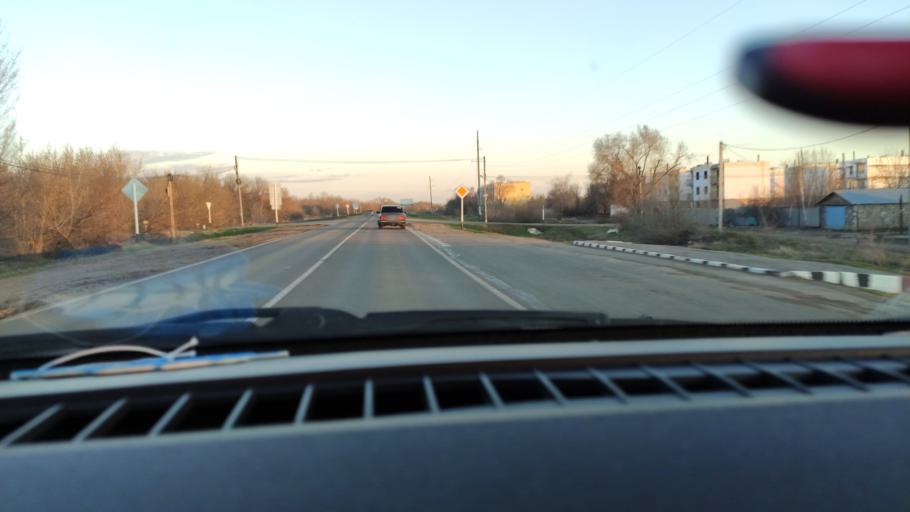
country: RU
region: Saratov
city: Privolzhskiy
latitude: 51.3832
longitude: 46.0414
